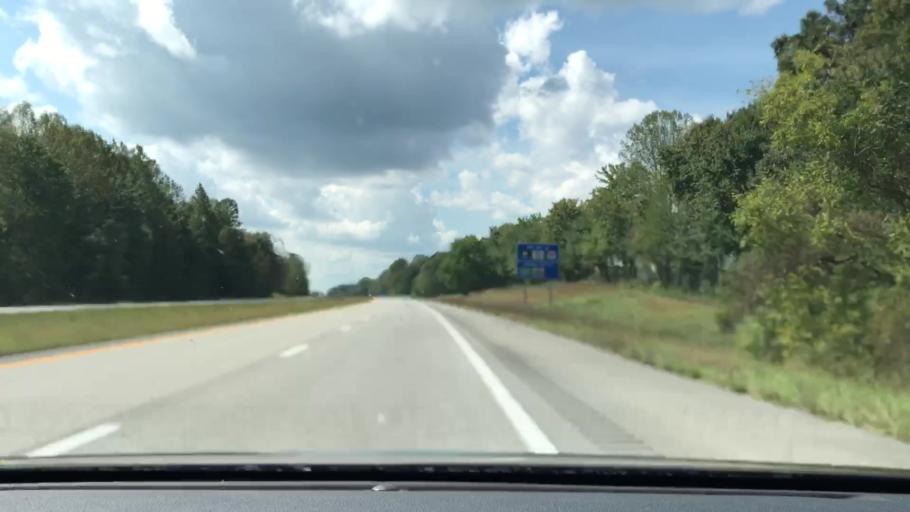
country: US
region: Kentucky
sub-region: Russell County
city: Russell Springs
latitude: 37.0683
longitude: -85.0417
